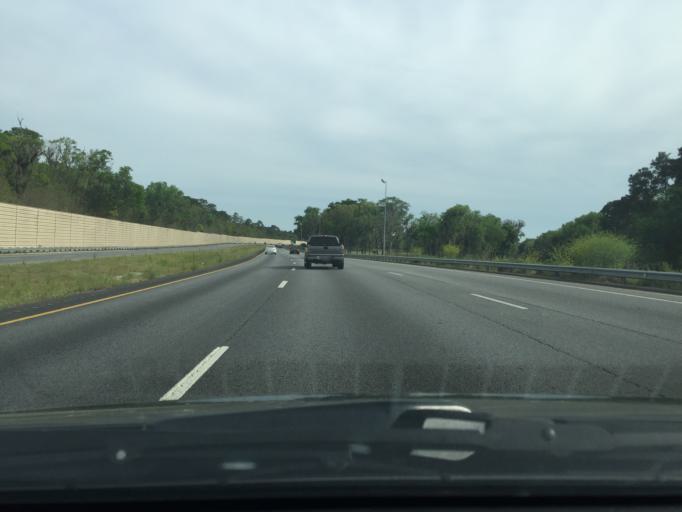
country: US
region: Georgia
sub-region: Chatham County
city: Thunderbolt
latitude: 32.0183
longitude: -81.0879
